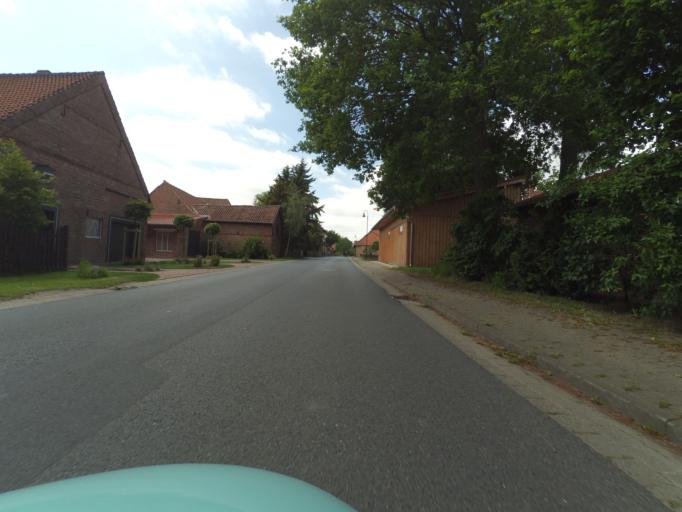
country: DE
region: Lower Saxony
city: Dollbergen
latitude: 52.4104
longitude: 10.1380
